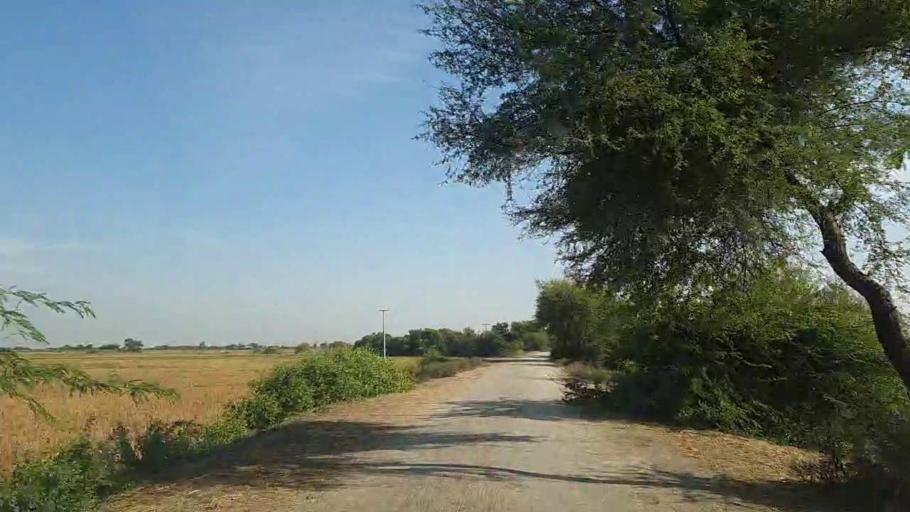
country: PK
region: Sindh
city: Bulri
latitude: 24.7952
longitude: 68.3404
